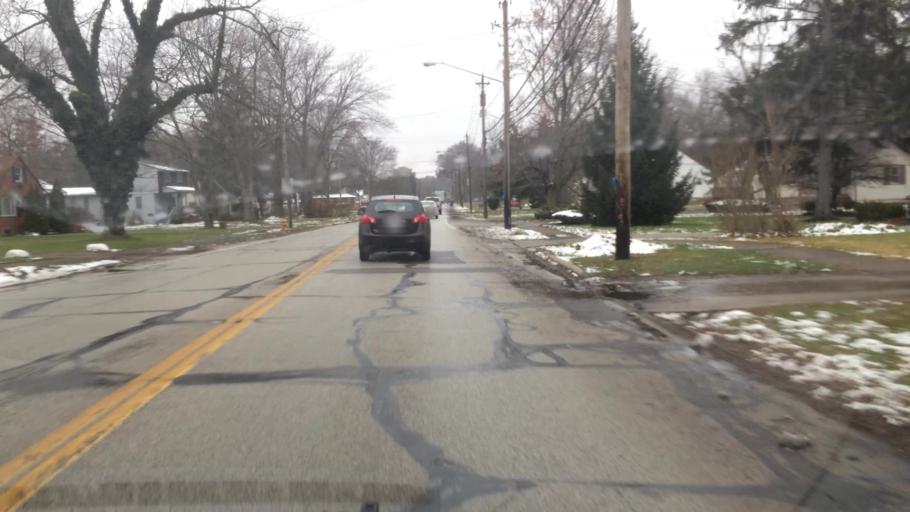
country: US
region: Ohio
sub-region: Cuyahoga County
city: North Olmsted
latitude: 41.4273
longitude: -81.8966
